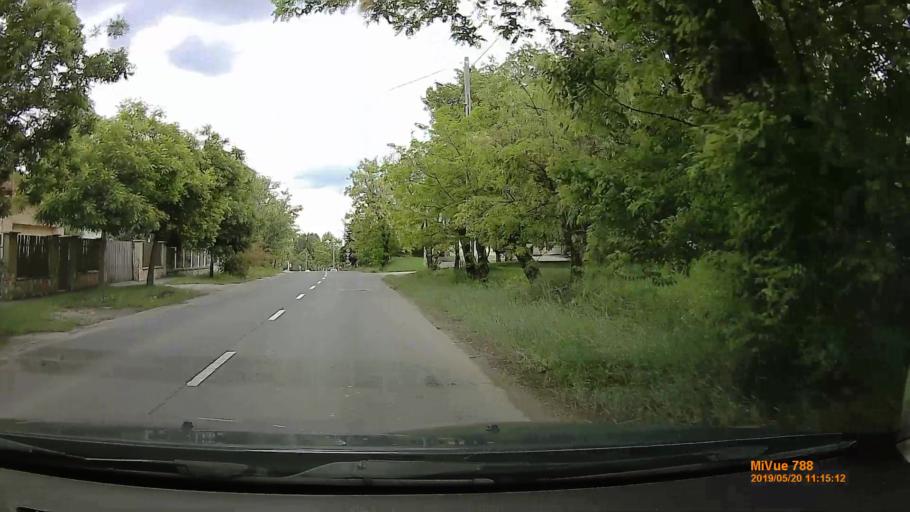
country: HU
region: Pest
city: Ecser
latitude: 47.4673
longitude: 19.2962
